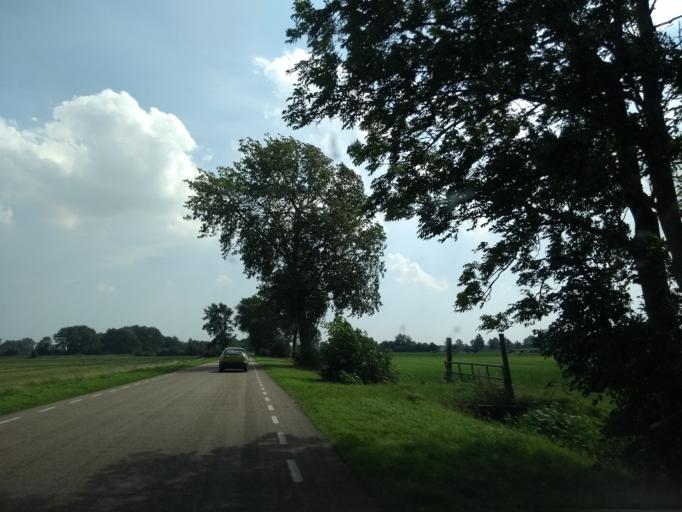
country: NL
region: Friesland
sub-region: Sudwest Fryslan
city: Oppenhuizen
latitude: 53.0373
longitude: 5.7148
